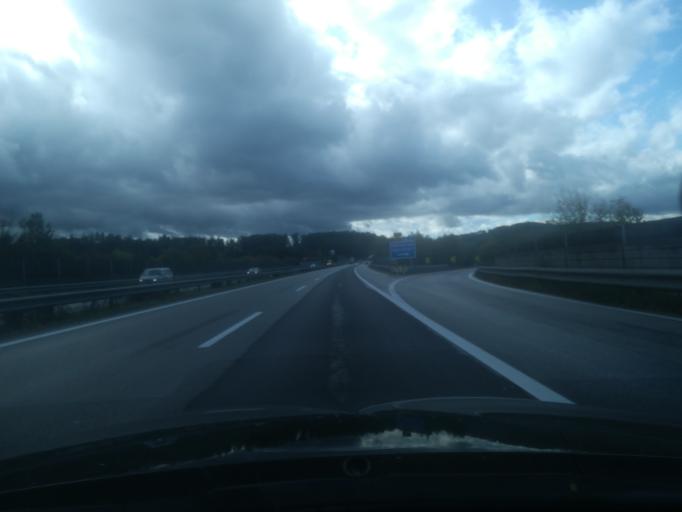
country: AT
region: Upper Austria
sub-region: Politischer Bezirk Urfahr-Umgebung
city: Engerwitzdorf
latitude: 48.3434
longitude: 14.4493
